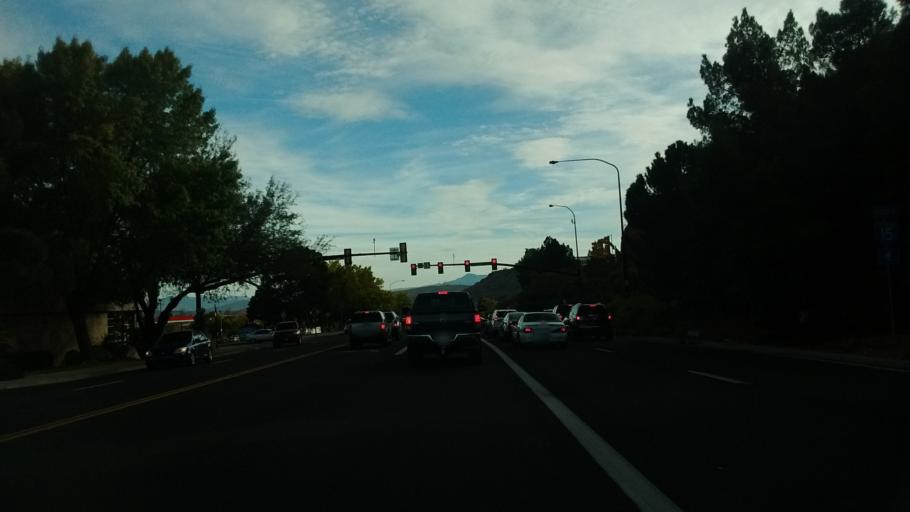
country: US
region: Utah
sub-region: Washington County
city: Saint George
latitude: 37.1106
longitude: -113.5942
